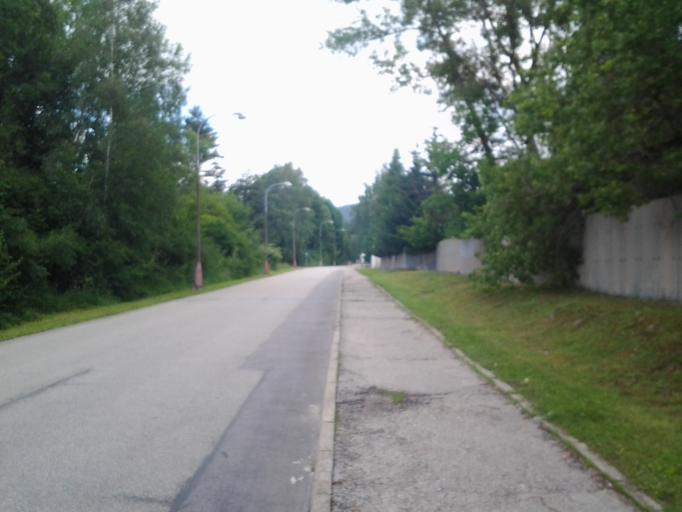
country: CZ
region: Jihocesky
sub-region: Okres Cesky Krumlov
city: Cesky Krumlov
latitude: 48.8251
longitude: 14.3085
